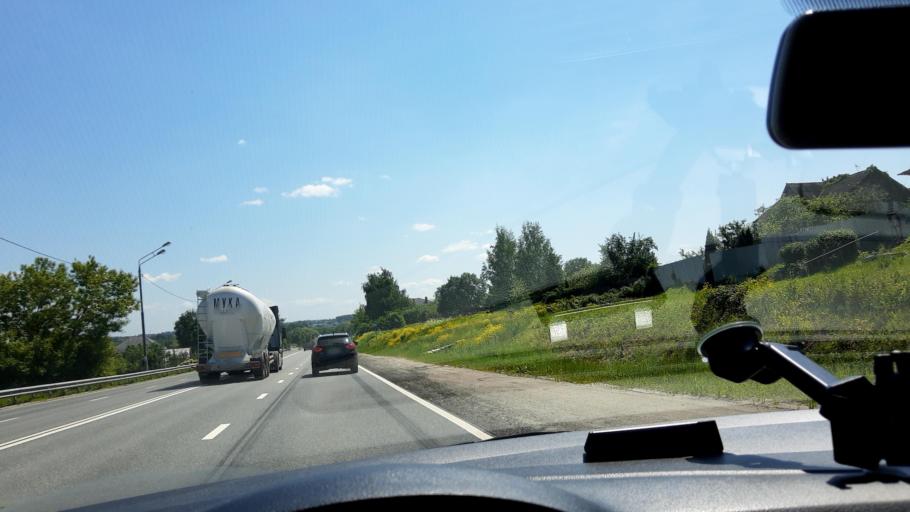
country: RU
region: Moskovskaya
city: Bronnitsy
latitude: 55.4443
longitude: 38.2122
